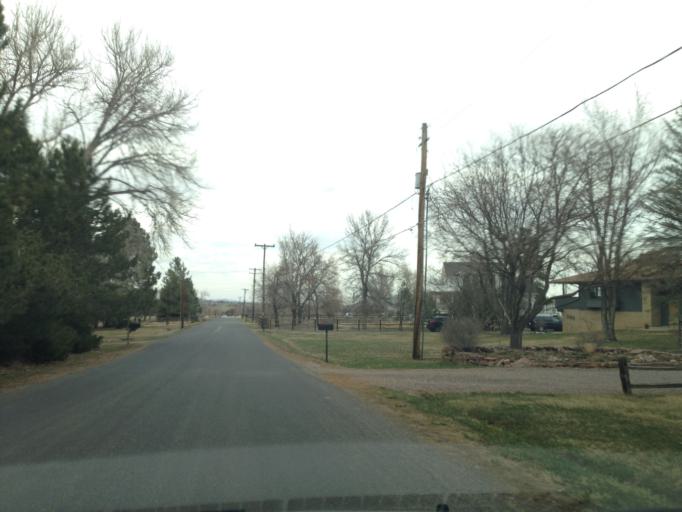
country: US
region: Colorado
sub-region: Boulder County
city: Superior
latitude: 39.9803
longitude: -105.1940
